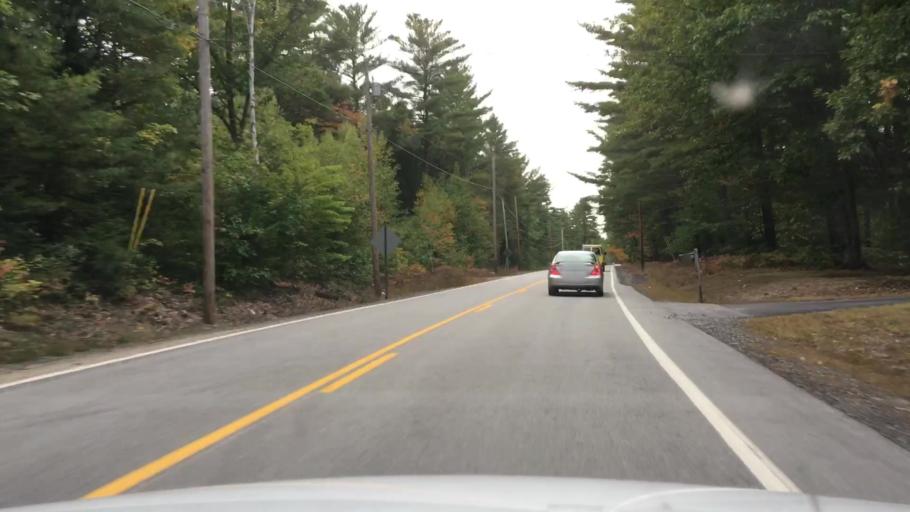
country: US
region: Maine
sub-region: Cumberland County
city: Harrison
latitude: 44.2134
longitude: -70.6816
